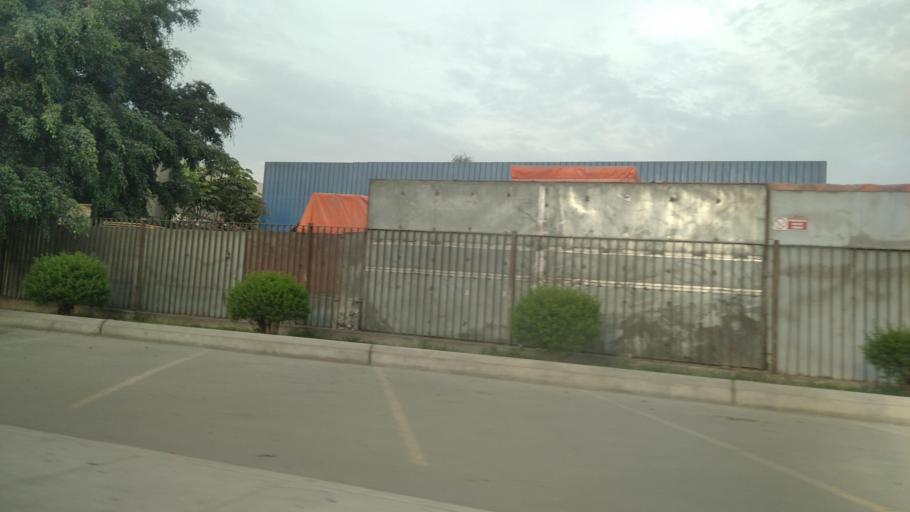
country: PE
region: Lima
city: Lima
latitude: -12.0214
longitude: -76.9976
